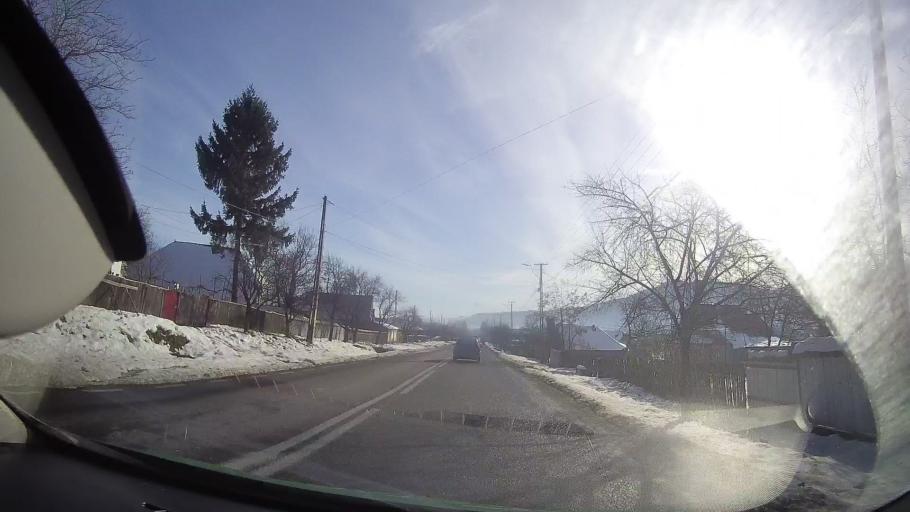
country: RO
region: Neamt
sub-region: Comuna Cracaoani
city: Cracaoani
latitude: 47.1027
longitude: 26.3075
